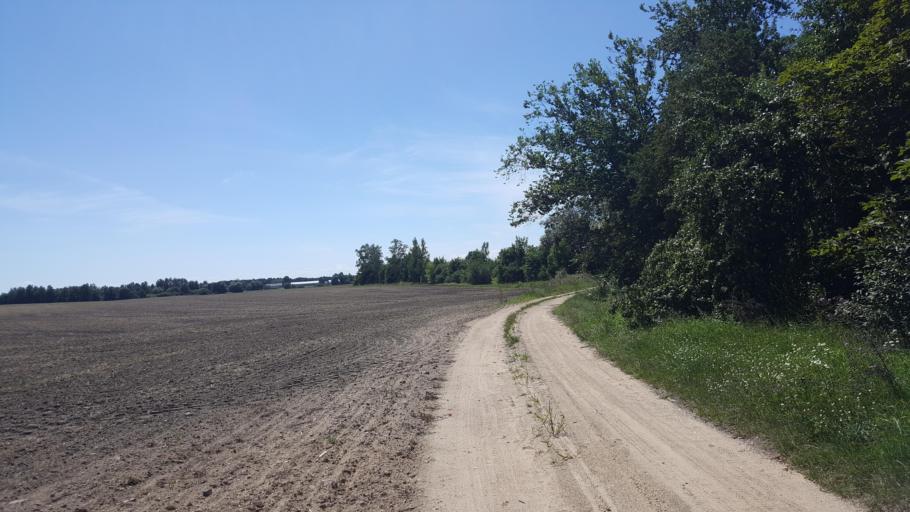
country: BY
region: Brest
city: Charnawchytsy
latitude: 52.2358
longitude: 23.7855
